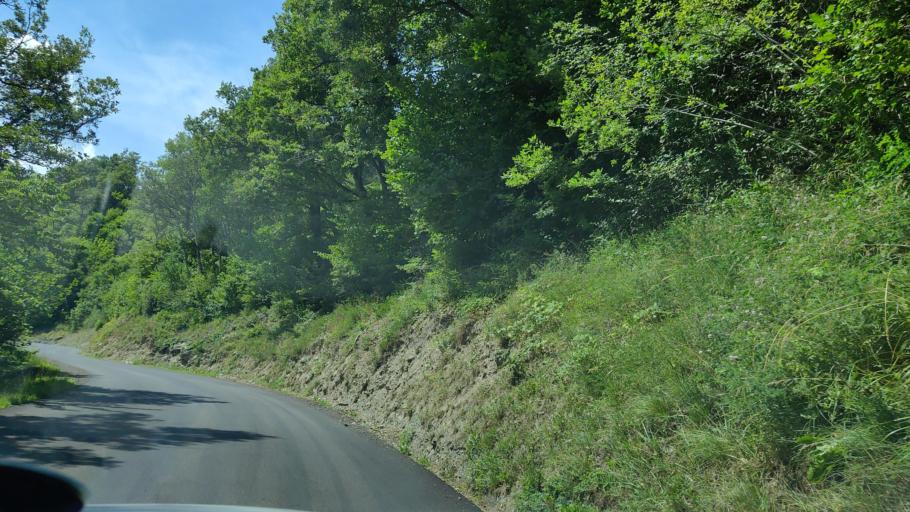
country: FR
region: Rhone-Alpes
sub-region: Departement de la Savoie
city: Saint-Bon-Tarentaise
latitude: 45.4515
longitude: 6.6029
